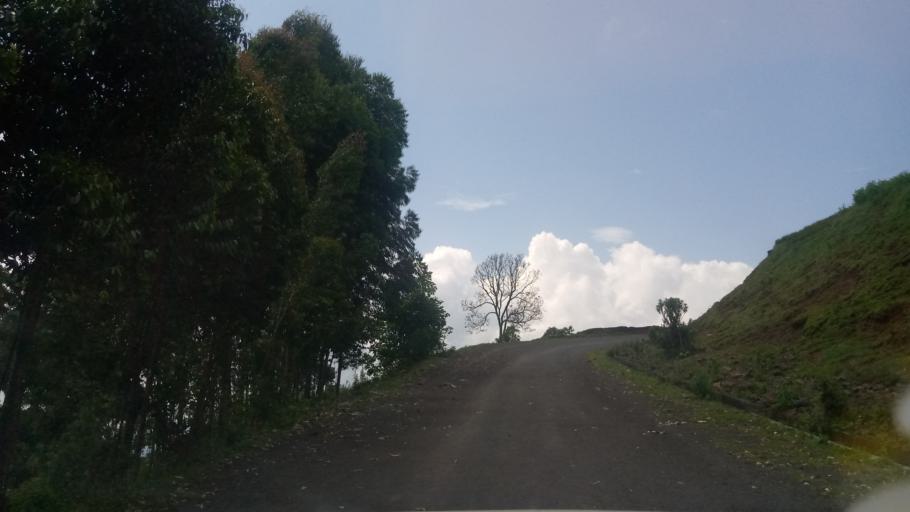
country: ET
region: Southern Nations, Nationalities, and People's Region
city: Bonga
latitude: 7.1459
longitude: 36.5753
